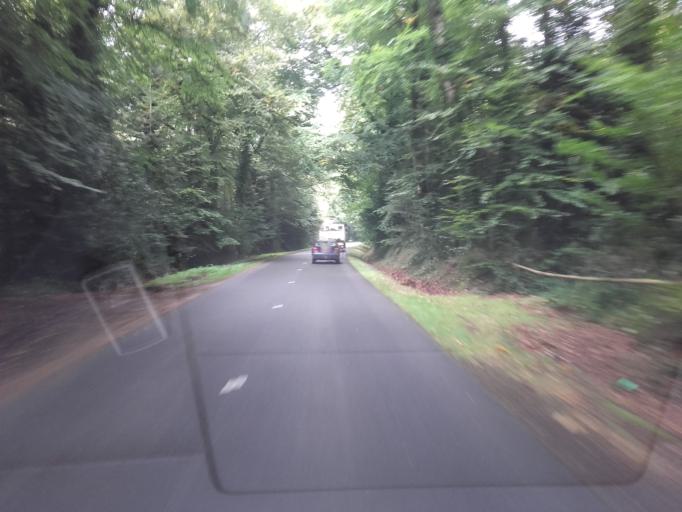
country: FR
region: Brittany
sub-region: Departement des Cotes-d'Armor
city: Plelo
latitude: 48.5877
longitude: -2.9469
